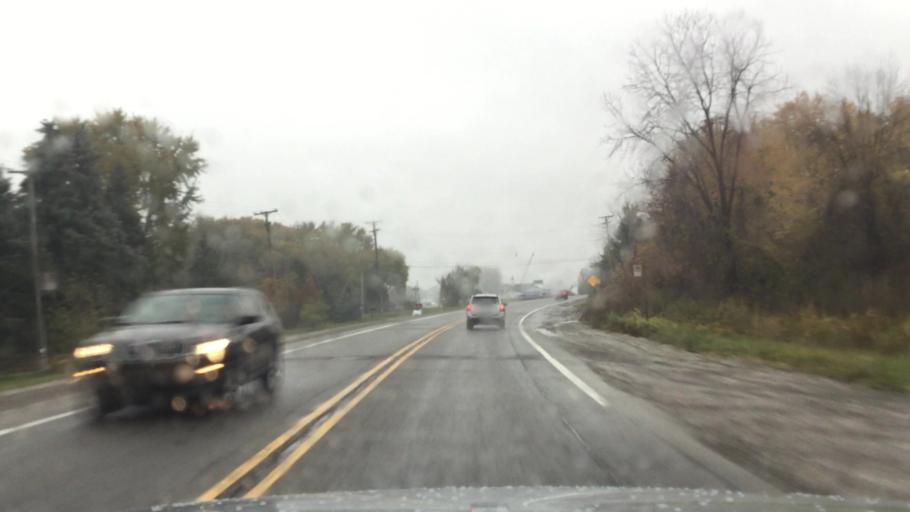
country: US
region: Michigan
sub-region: Macomb County
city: New Baltimore
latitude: 42.6585
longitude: -82.7744
